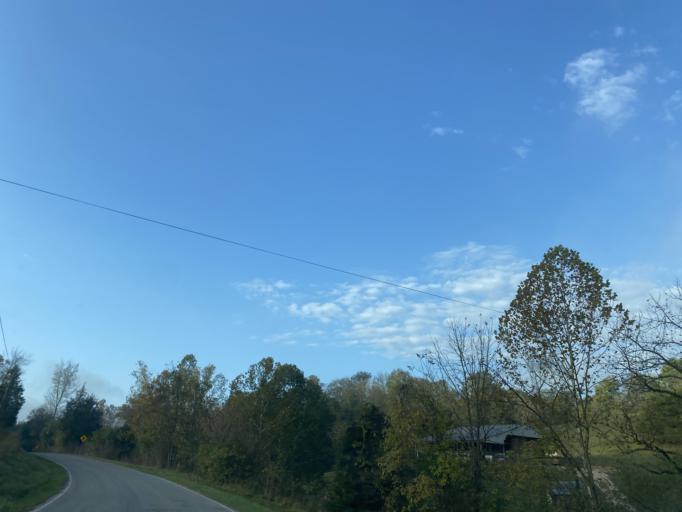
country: US
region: Kentucky
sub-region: Pendleton County
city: Falmouth
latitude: 38.7285
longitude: -84.3191
